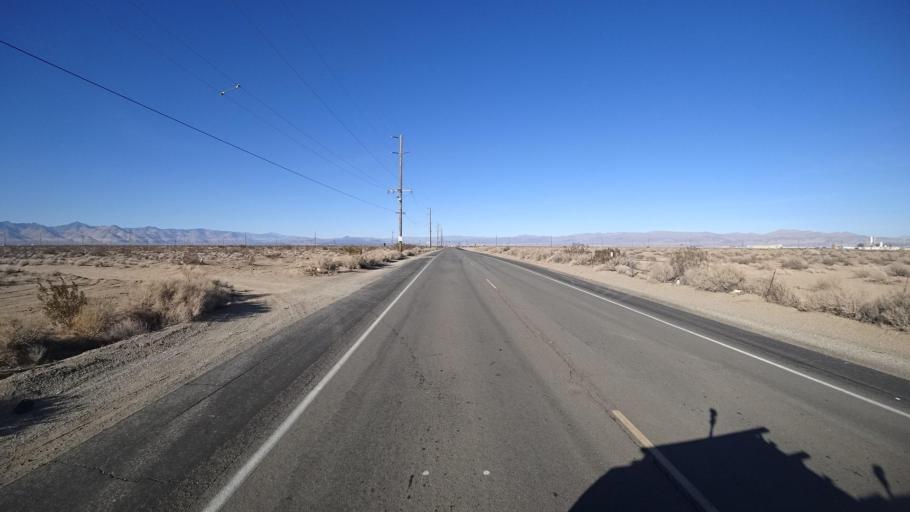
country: US
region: California
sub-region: Kern County
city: China Lake Acres
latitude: 35.6480
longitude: -117.7231
